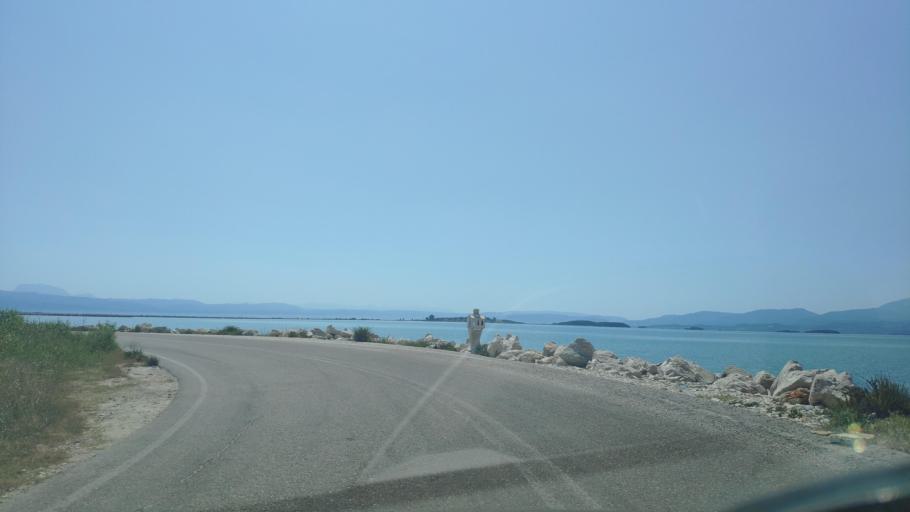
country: GR
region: Epirus
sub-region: Nomos Artas
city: Aneza
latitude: 39.0336
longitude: 20.8848
